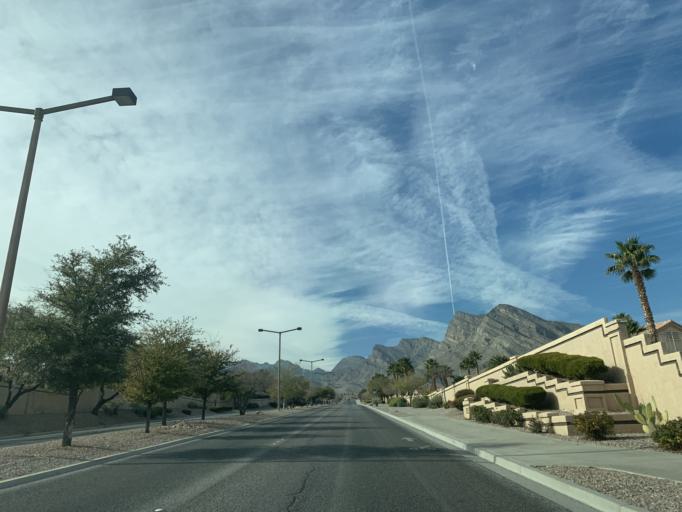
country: US
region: Nevada
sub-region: Clark County
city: Summerlin South
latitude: 36.2044
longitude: -115.3344
